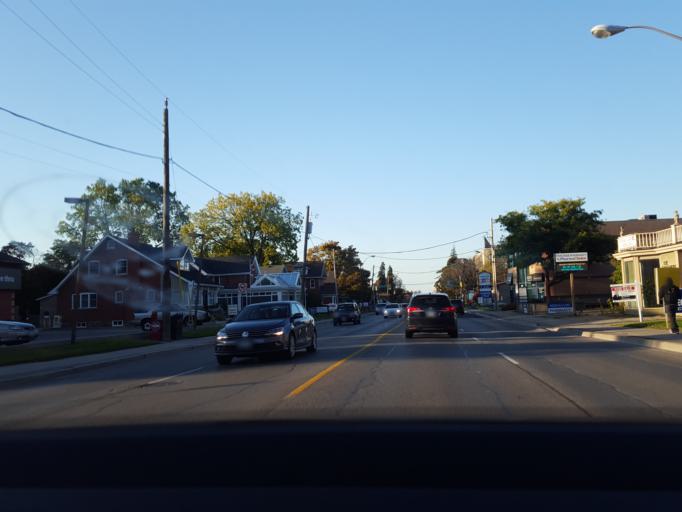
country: CA
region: Ontario
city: Newmarket
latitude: 43.9926
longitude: -79.4658
